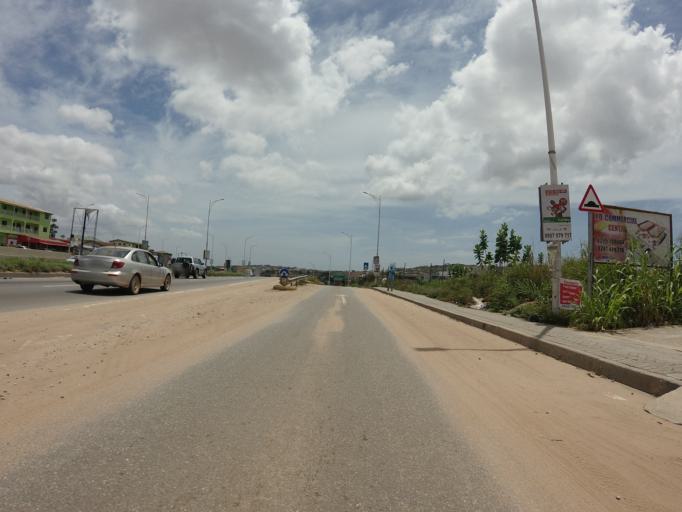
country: GH
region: Greater Accra
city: Gbawe
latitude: 5.5466
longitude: -0.3461
